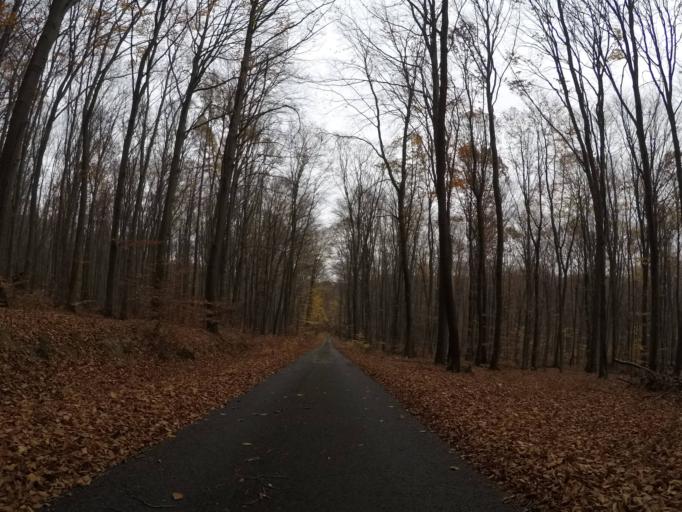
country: SK
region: Presovsky
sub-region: Okres Presov
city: Presov
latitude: 48.8836
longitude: 21.1955
